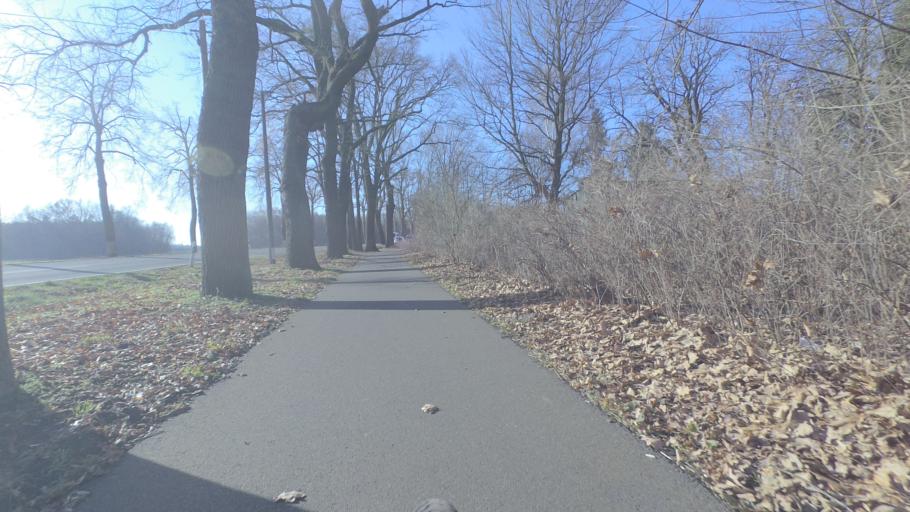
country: DE
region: Brandenburg
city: Luckenwalde
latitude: 52.1073
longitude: 13.1940
